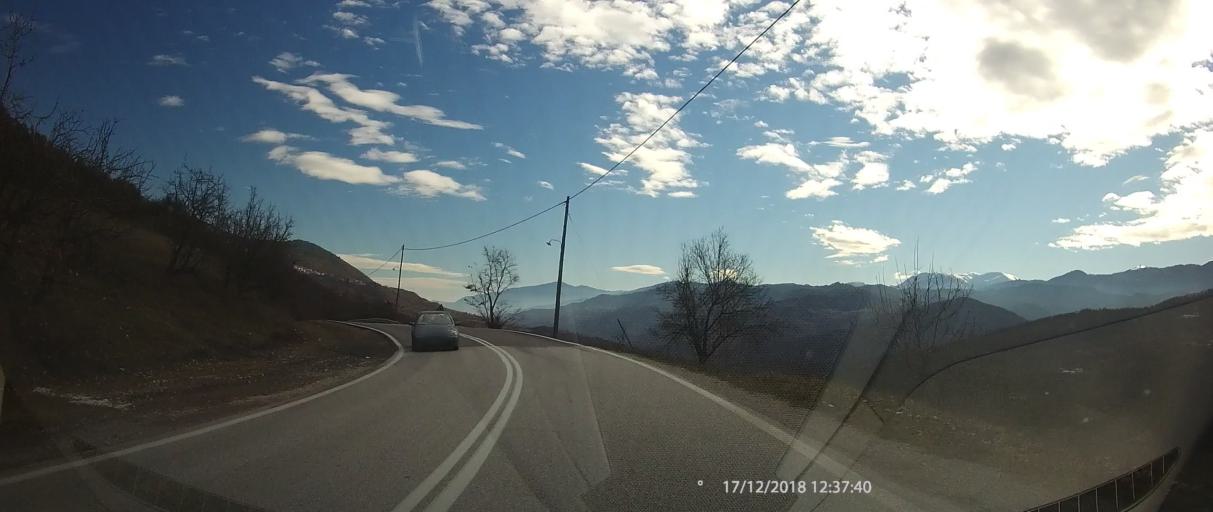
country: GR
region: Epirus
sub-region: Nomos Ioanninon
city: Metsovo
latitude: 39.8095
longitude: 21.3388
